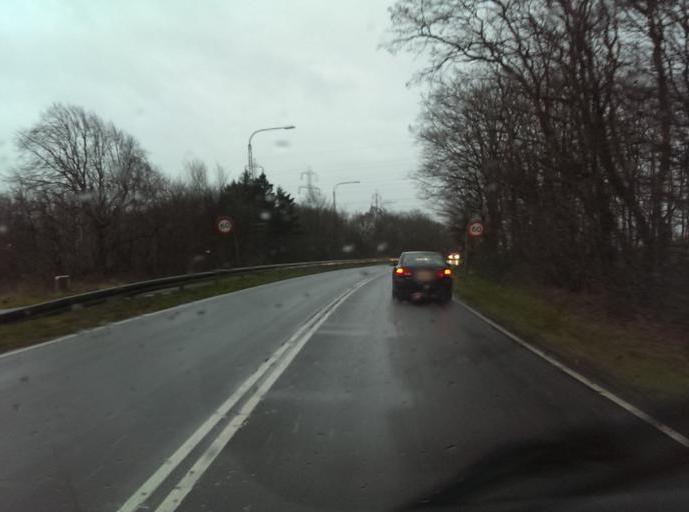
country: DK
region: South Denmark
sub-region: Esbjerg Kommune
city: Esbjerg
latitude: 55.4821
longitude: 8.5024
